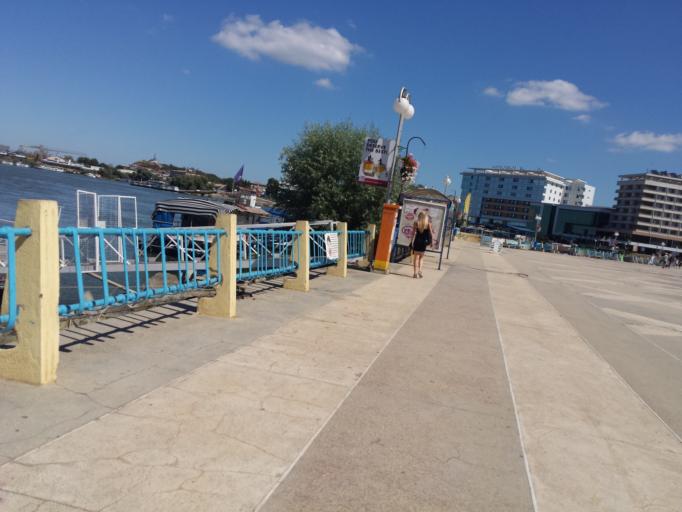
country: RO
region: Tulcea
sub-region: Municipiul Tulcea
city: Tulcea
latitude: 45.1802
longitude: 28.8006
